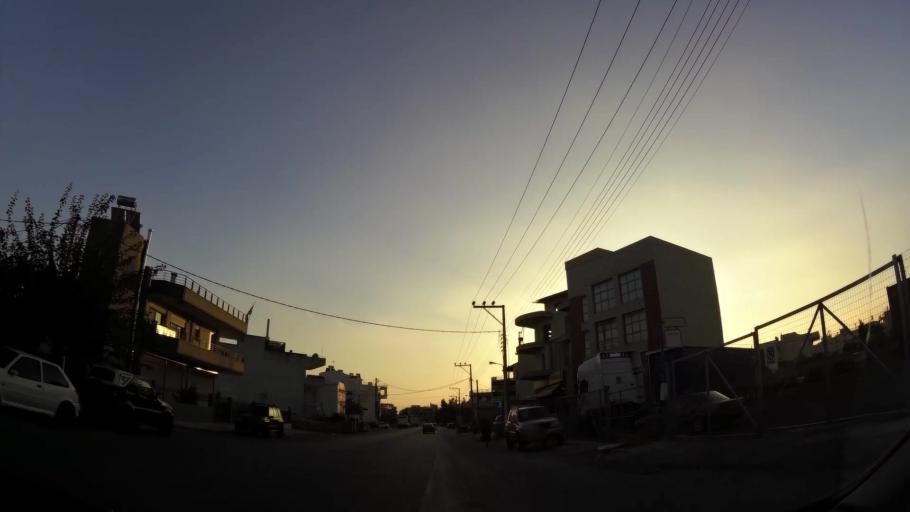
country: GR
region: Attica
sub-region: Nomarchia Anatolikis Attikis
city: Acharnes
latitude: 38.0916
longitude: 23.7456
